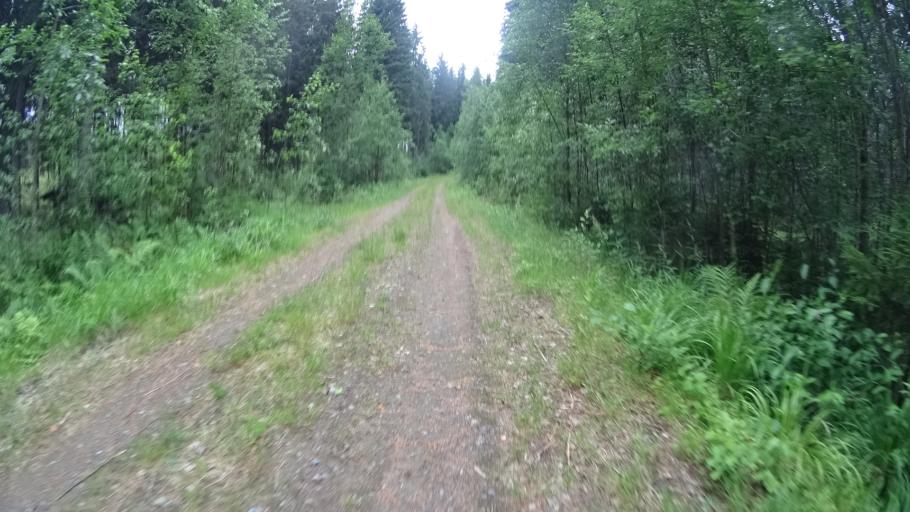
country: FI
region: Uusimaa
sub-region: Helsinki
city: Karkkila
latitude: 60.5674
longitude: 24.3334
